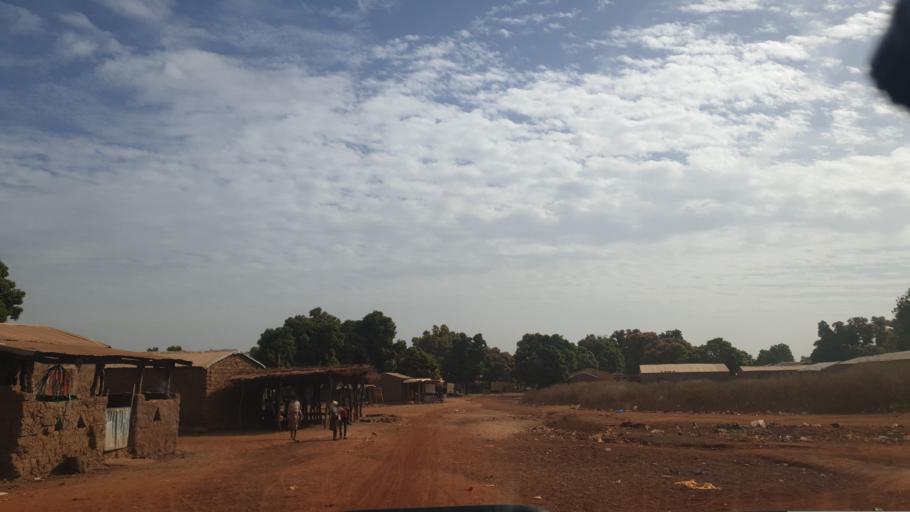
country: ML
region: Sikasso
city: Yanfolila
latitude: 11.4184
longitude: -7.9969
